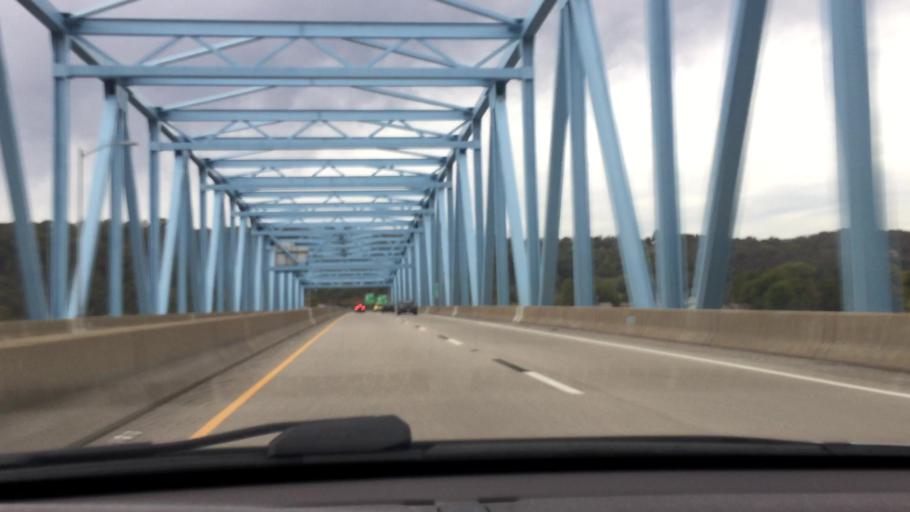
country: US
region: Pennsylvania
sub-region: Beaver County
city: Beaver
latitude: 40.6788
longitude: -80.3313
